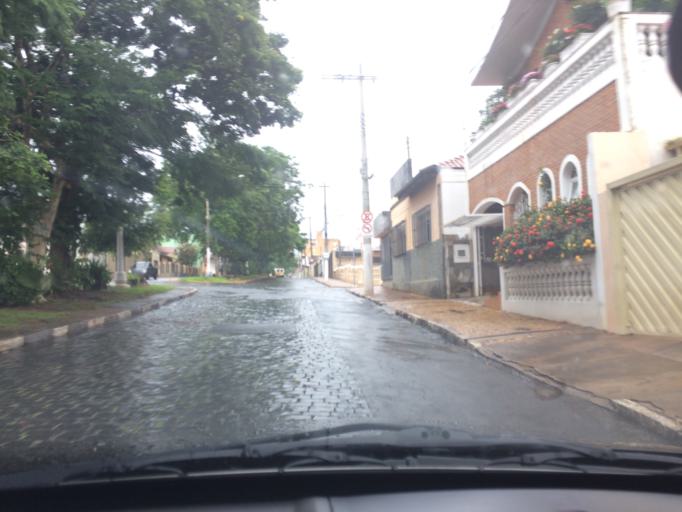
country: BR
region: Sao Paulo
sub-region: Casa Branca
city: Casa Branca
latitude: -21.7730
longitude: -47.0887
